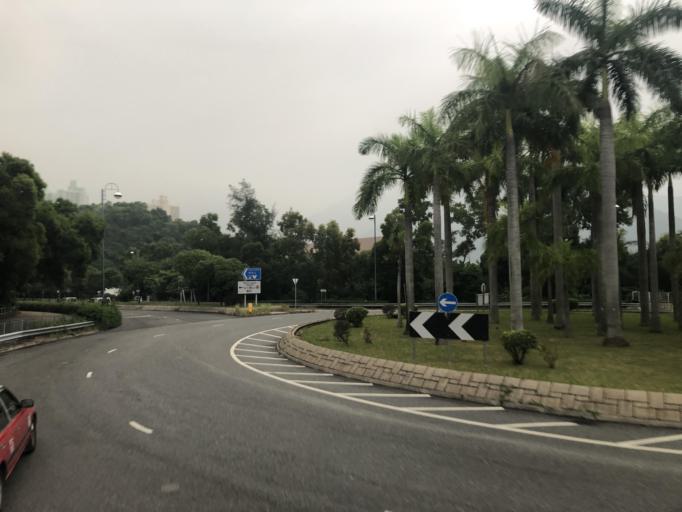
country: HK
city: Tai O
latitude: 22.2905
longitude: 113.9374
